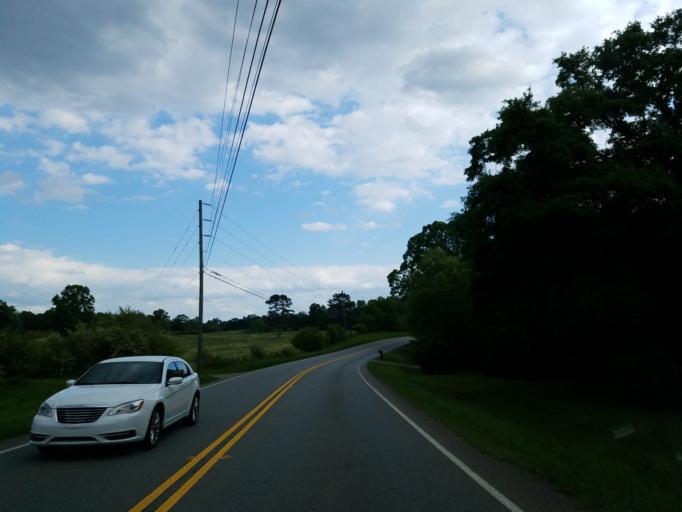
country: US
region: Georgia
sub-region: Fulton County
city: Milton
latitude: 34.2472
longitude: -84.2855
